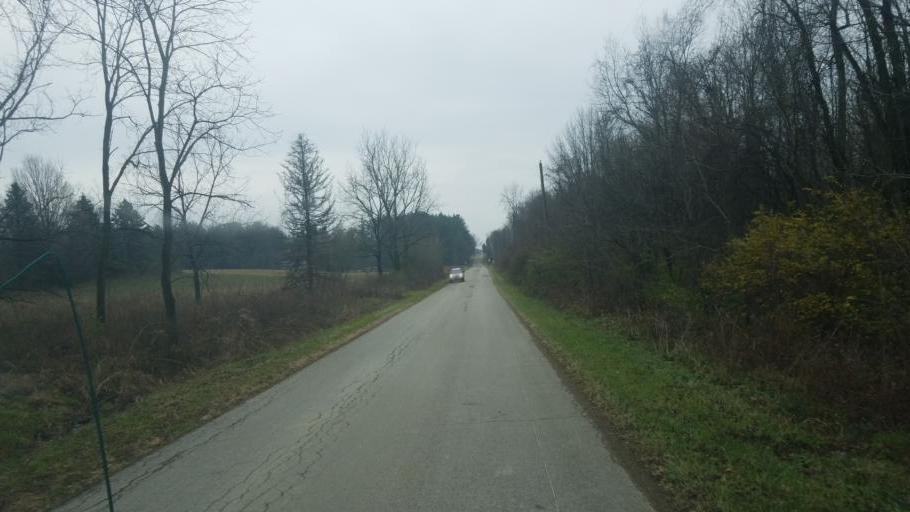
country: US
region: Ohio
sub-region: Crawford County
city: Crestline
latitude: 40.6917
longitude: -82.6894
